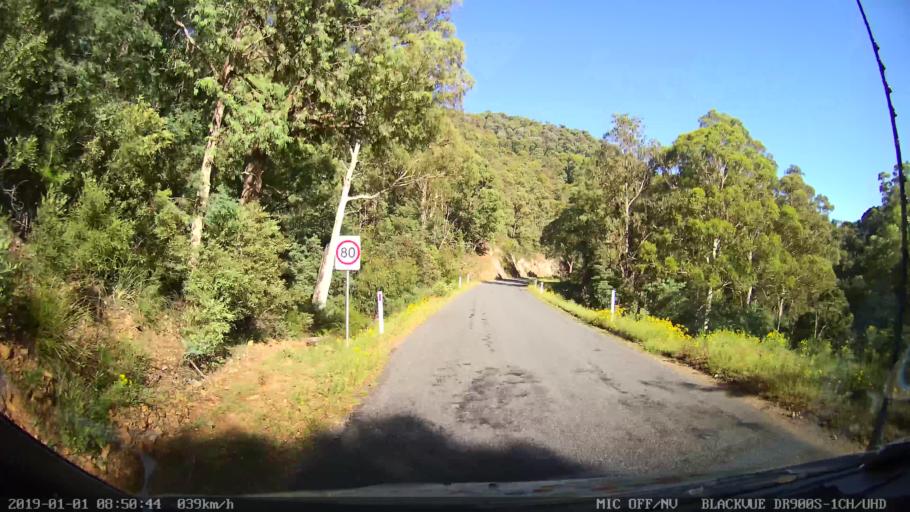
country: AU
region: New South Wales
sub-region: Snowy River
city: Jindabyne
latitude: -36.2751
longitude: 148.2016
